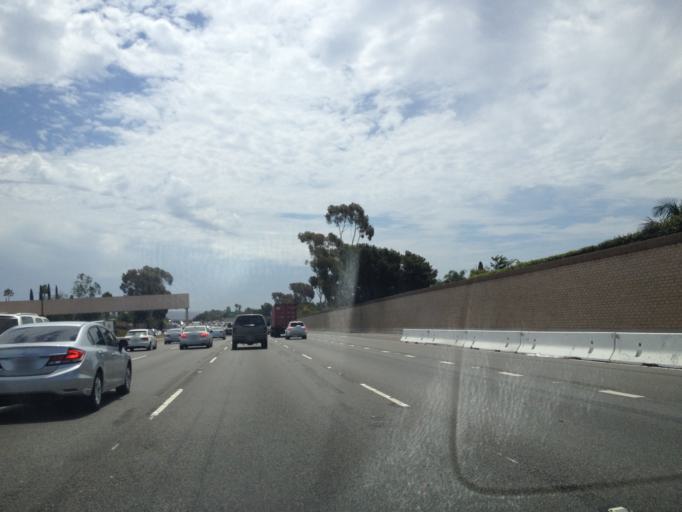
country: US
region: California
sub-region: Orange County
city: Dana Point
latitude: 33.4634
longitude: -117.6644
